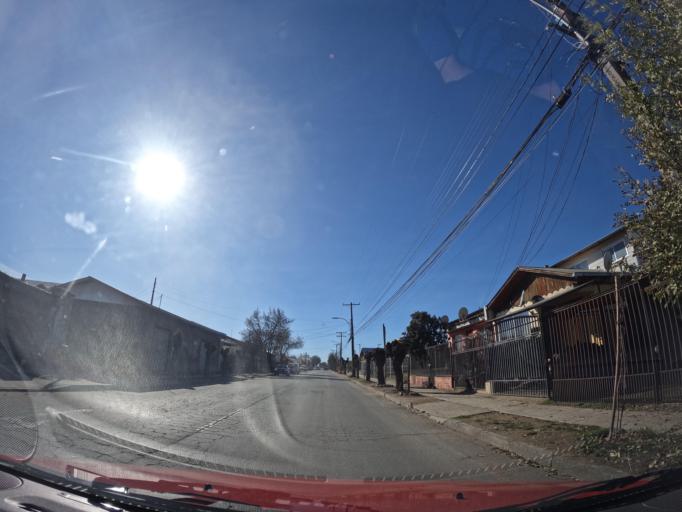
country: CL
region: Maule
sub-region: Provincia de Cauquenes
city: Cauquenes
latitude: -35.9849
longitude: -72.3182
